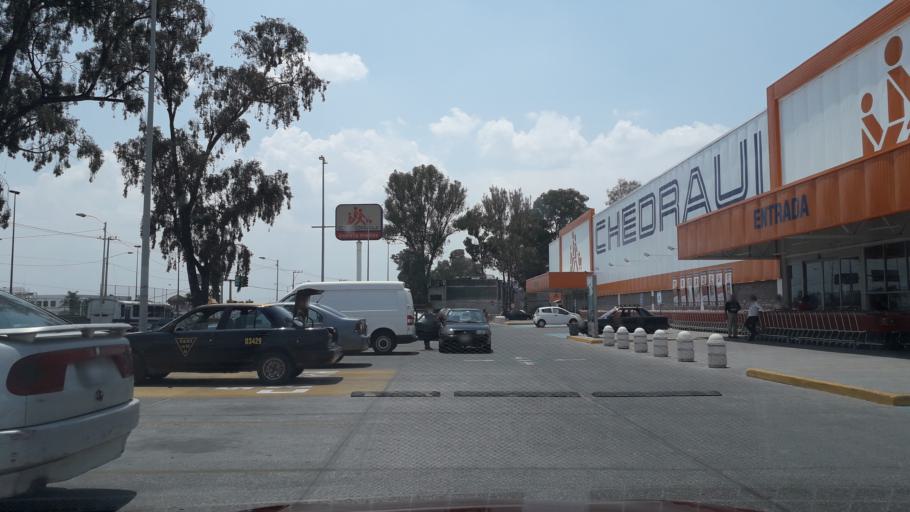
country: MX
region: Puebla
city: Puebla
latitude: 19.0496
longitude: -98.1698
